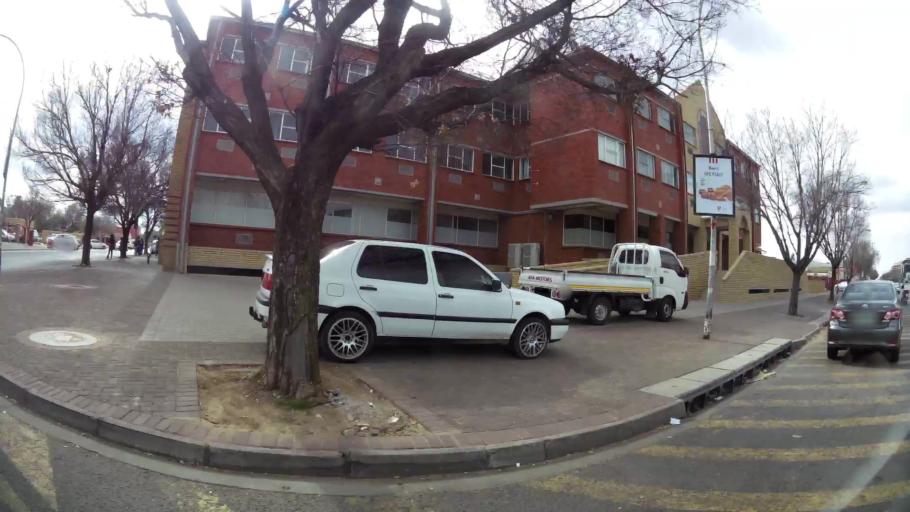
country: ZA
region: Orange Free State
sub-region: Mangaung Metropolitan Municipality
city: Bloemfontein
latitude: -29.1099
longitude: 26.2049
